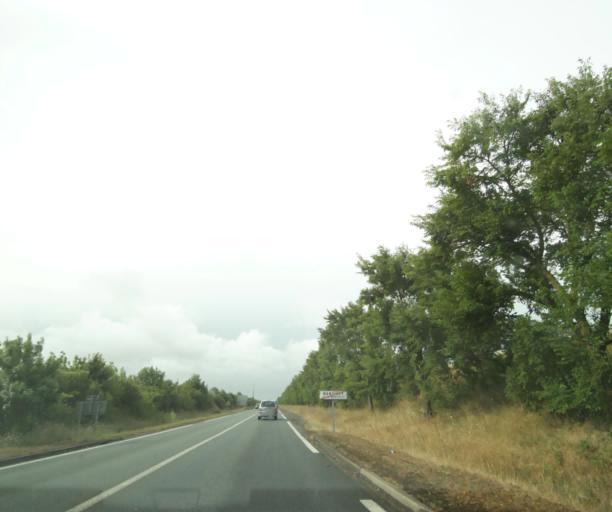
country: FR
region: Poitou-Charentes
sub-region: Departement de la Charente-Maritime
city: Marsilly
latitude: 46.2312
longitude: -1.1240
